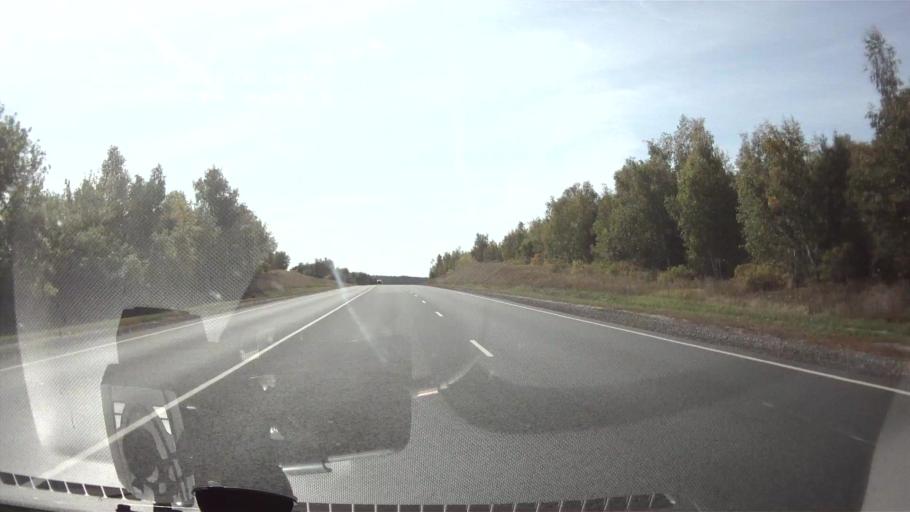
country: RU
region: Saratov
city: Khvalynsk
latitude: 52.5607
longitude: 48.0881
